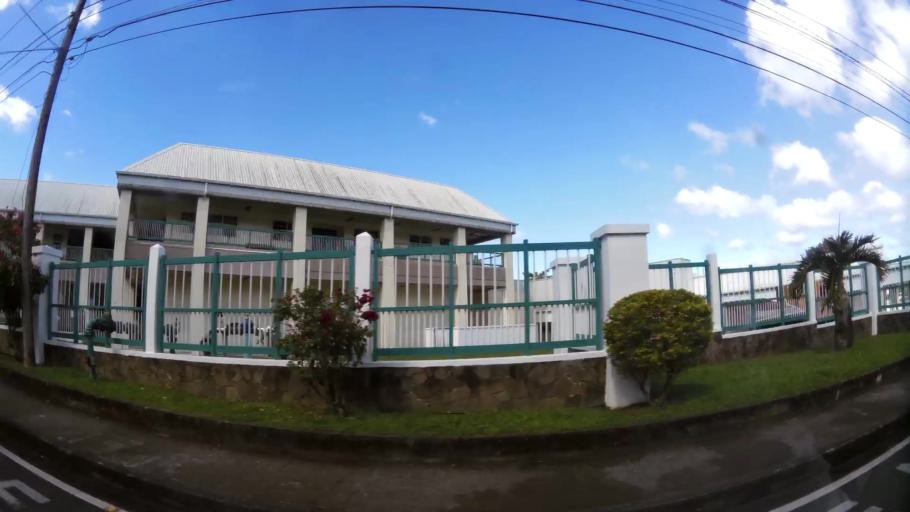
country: DM
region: Saint John
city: Portsmouth
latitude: 15.5572
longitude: -61.4579
